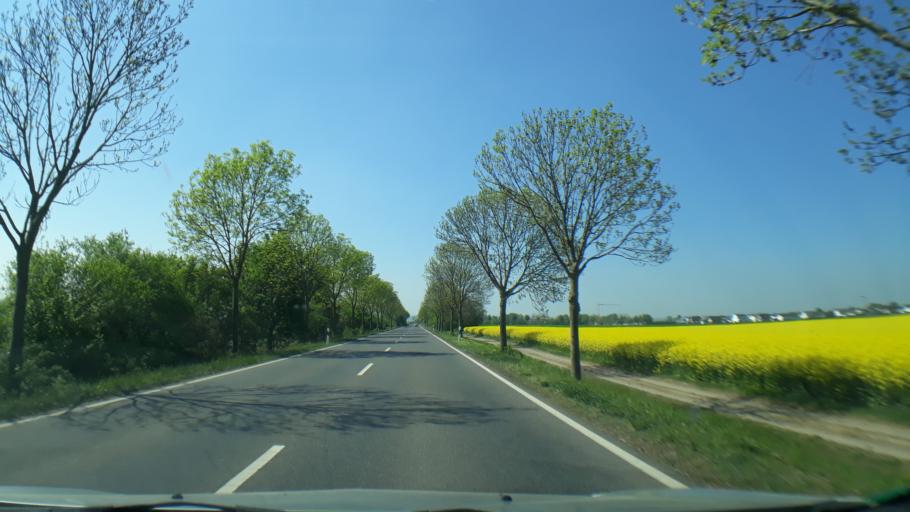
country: DE
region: North Rhine-Westphalia
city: Zulpich
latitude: 50.6890
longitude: 6.6710
